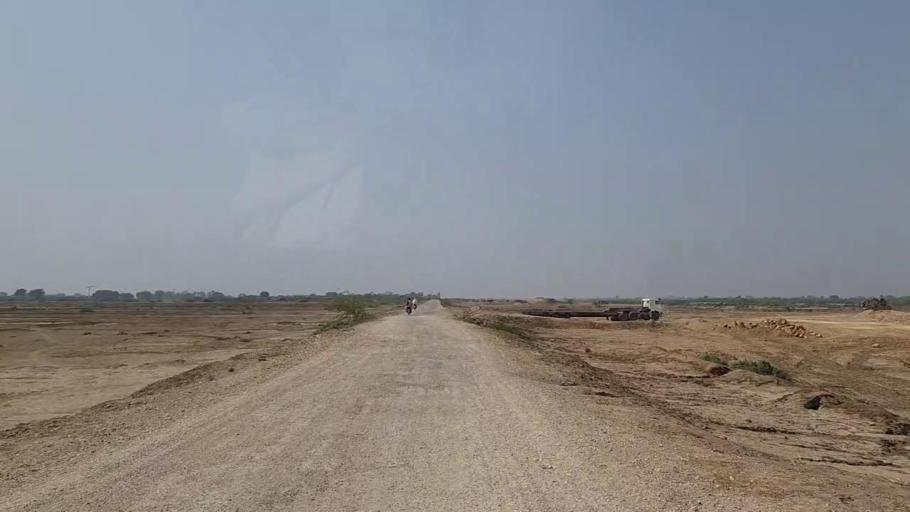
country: PK
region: Sindh
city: Naukot
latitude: 24.8299
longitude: 69.3897
